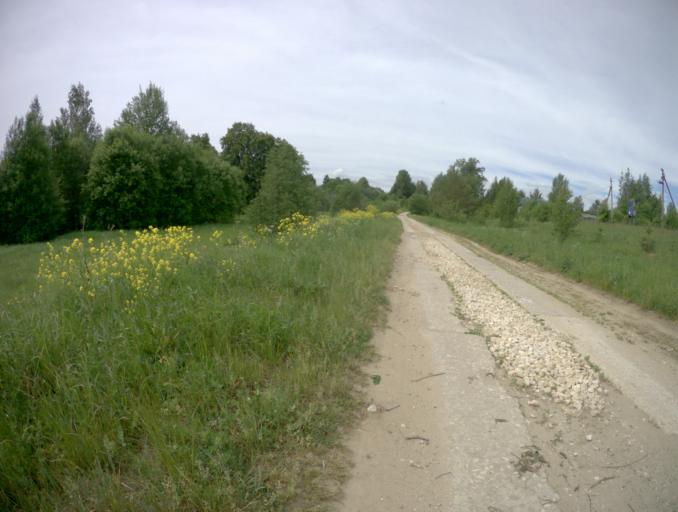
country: RU
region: Vladimir
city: Stavrovo
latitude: 56.1864
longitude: 39.9544
